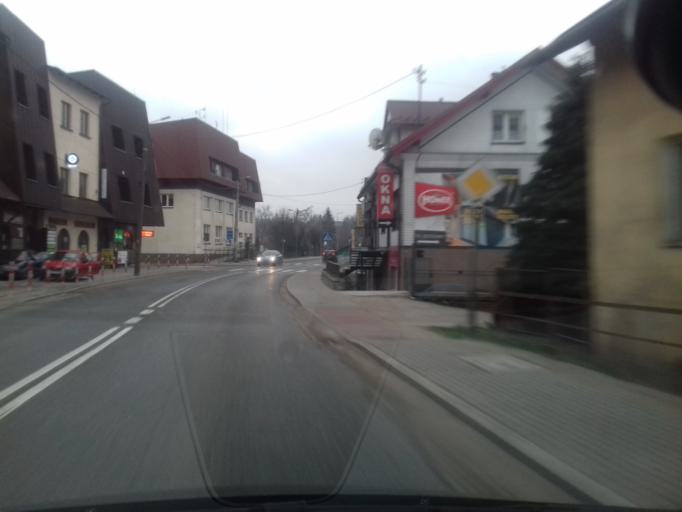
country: PL
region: Lesser Poland Voivodeship
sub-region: Powiat limanowski
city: Mszana Dolna
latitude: 49.6754
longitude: 20.0821
